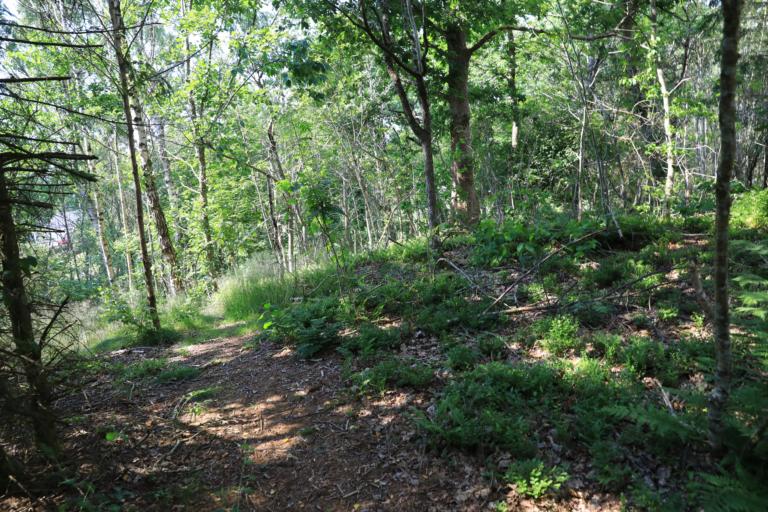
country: SE
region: Halland
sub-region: Varbergs Kommun
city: Varberg
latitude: 57.1715
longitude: 12.2922
